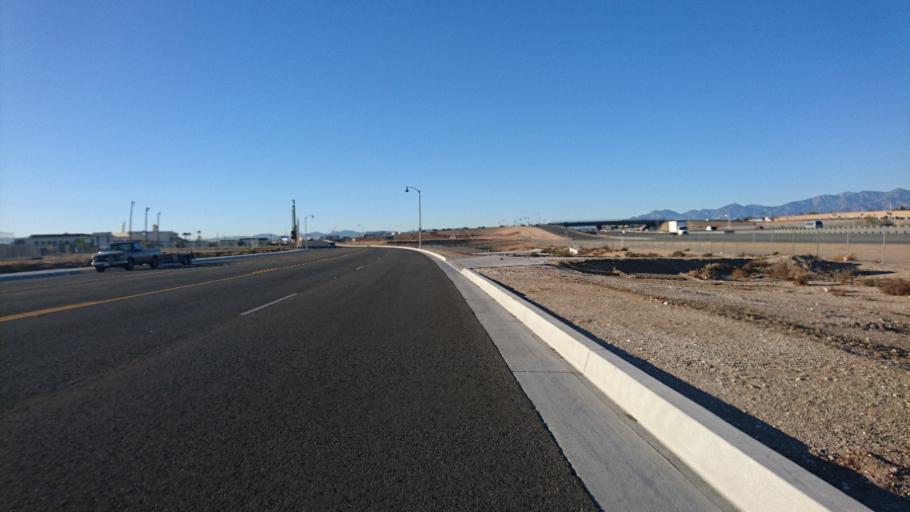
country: US
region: California
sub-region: San Bernardino County
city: Mountain View Acres
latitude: 34.4899
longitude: -117.3320
